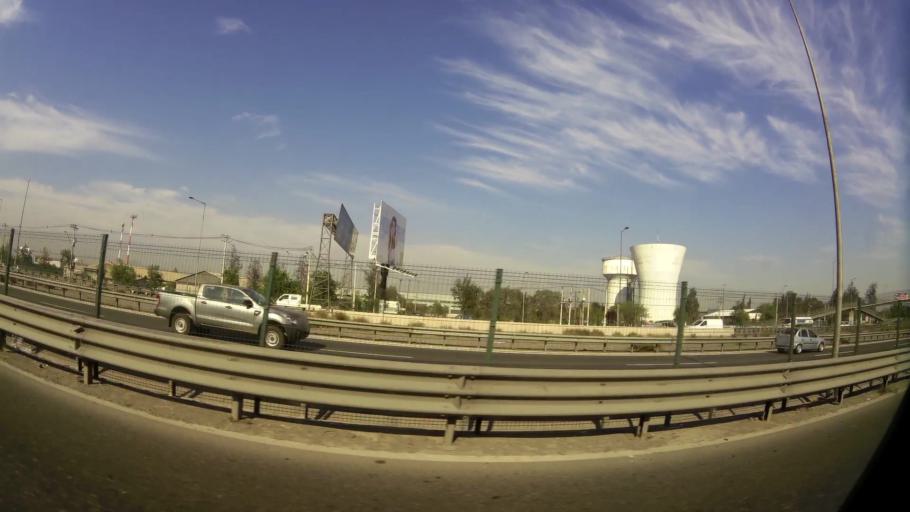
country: CL
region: Santiago Metropolitan
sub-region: Provincia de Santiago
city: Lo Prado
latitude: -33.5115
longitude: -70.7208
